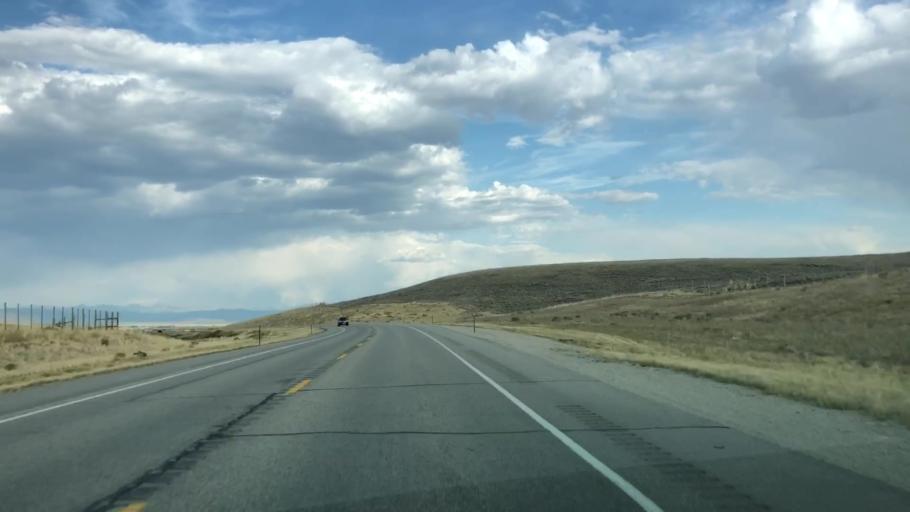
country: US
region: Wyoming
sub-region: Sublette County
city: Pinedale
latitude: 42.8760
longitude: -109.9507
